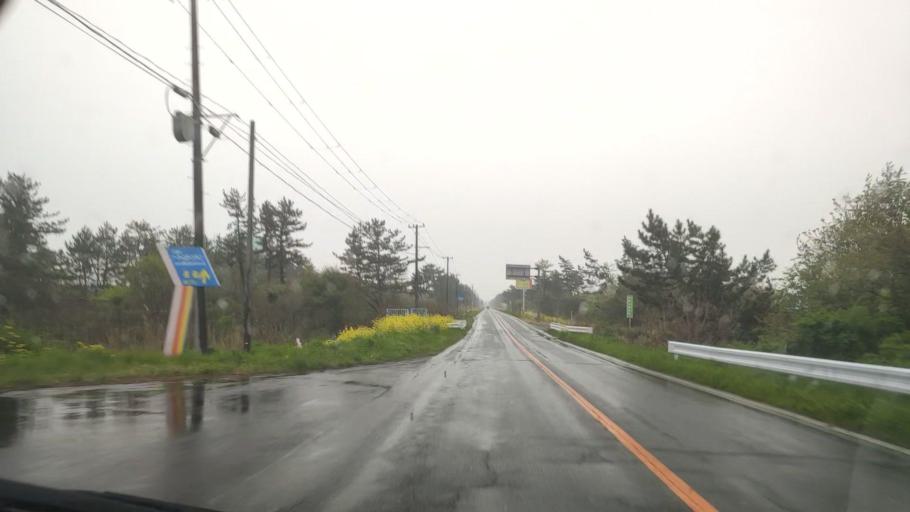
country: JP
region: Akita
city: Tenno
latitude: 40.0319
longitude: 139.9526
